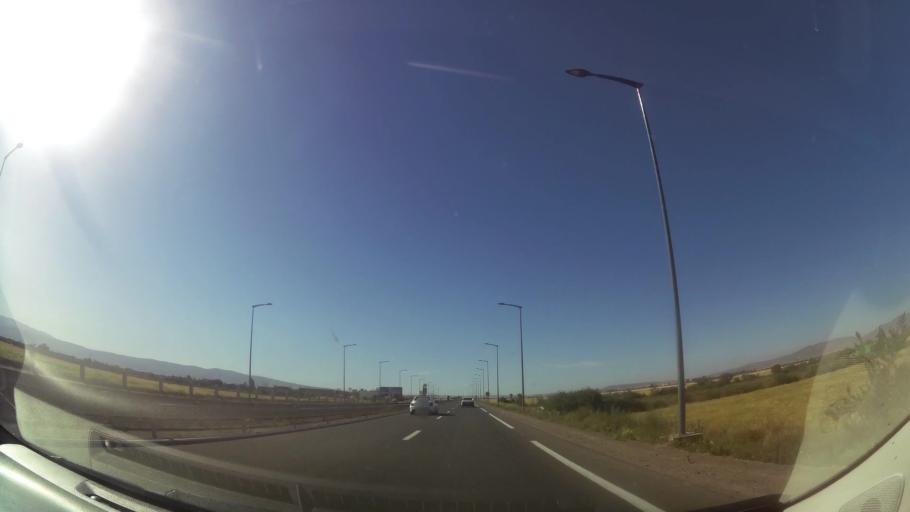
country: MA
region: Oriental
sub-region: Oujda-Angad
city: Oujda
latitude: 34.8042
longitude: -1.9574
